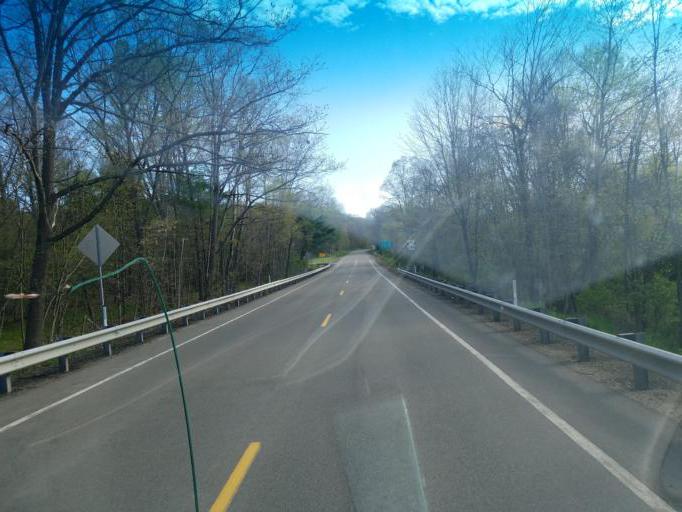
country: US
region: New York
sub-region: Allegany County
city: Wellsville
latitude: 41.9973
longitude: -77.8642
